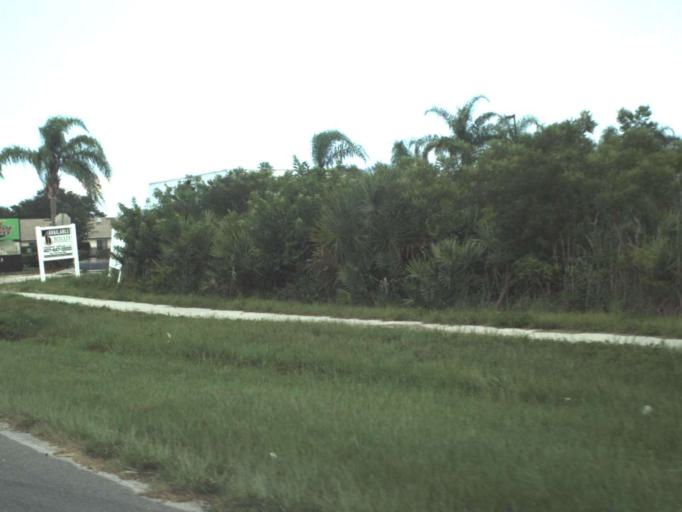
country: US
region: Florida
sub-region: Brevard County
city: June Park
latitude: 28.1213
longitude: -80.6761
